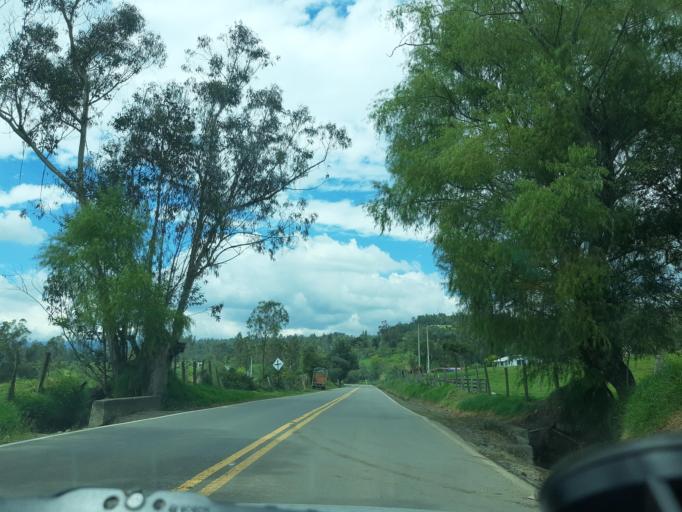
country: CO
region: Boyaca
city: Chiquinquira
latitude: 5.6169
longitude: -73.7466
